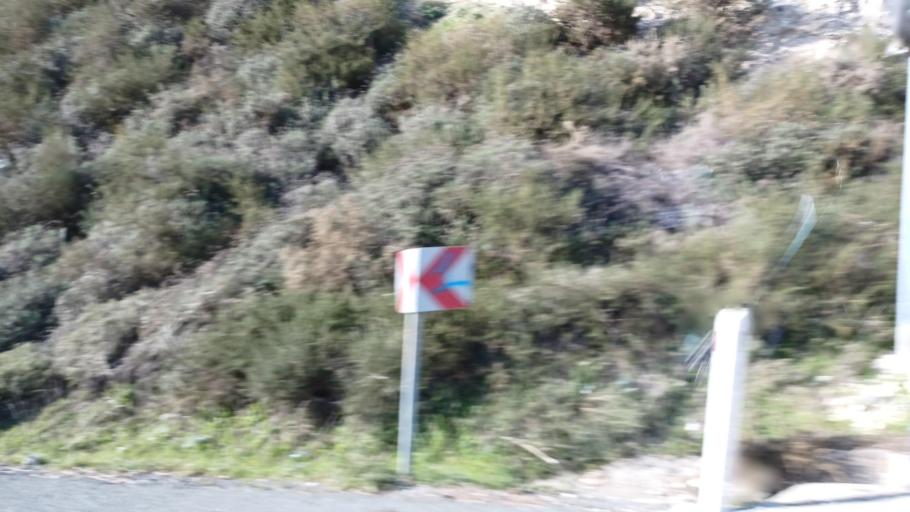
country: CY
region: Limassol
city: Pachna
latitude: 34.8102
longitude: 32.7934
